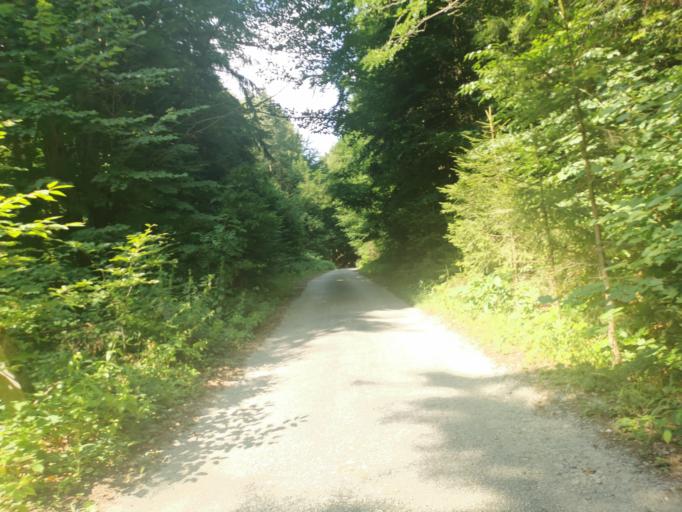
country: SK
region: Trenciansky
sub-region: Okres Myjava
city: Myjava
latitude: 48.8110
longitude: 17.5665
